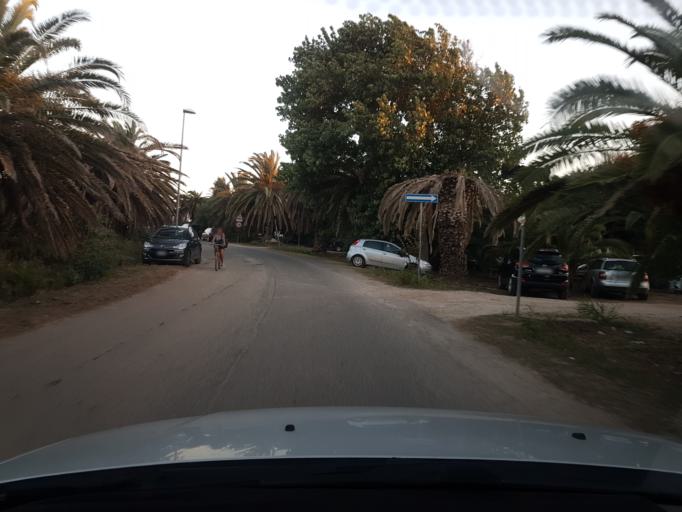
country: IT
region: Sardinia
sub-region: Provincia di Oristano
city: Riola Sardo
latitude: 40.0346
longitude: 8.3994
